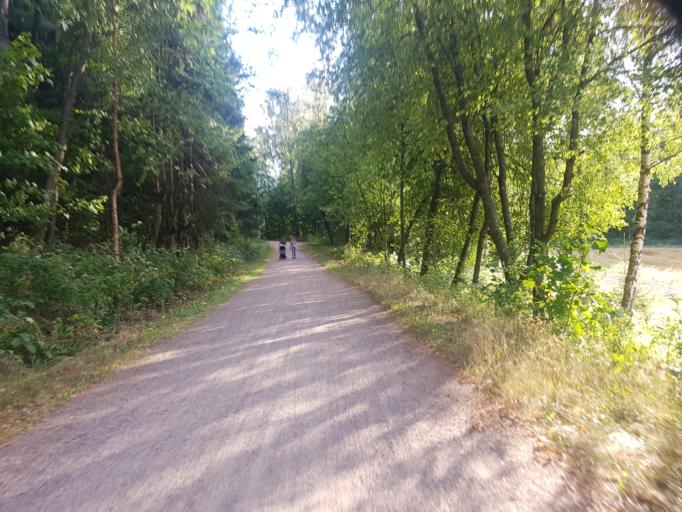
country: FI
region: Uusimaa
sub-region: Helsinki
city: Vantaa
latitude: 60.2523
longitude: 24.9641
